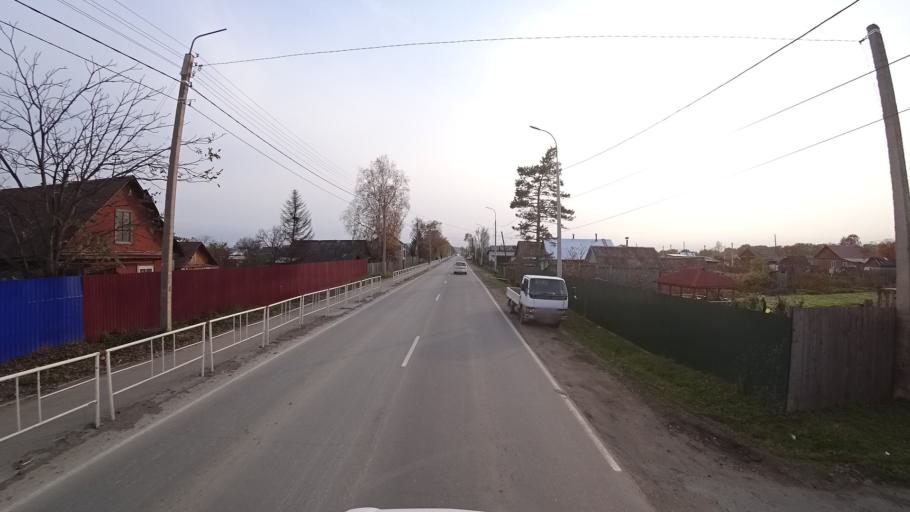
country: RU
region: Khabarovsk Krai
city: Amursk
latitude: 50.0954
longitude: 136.5060
